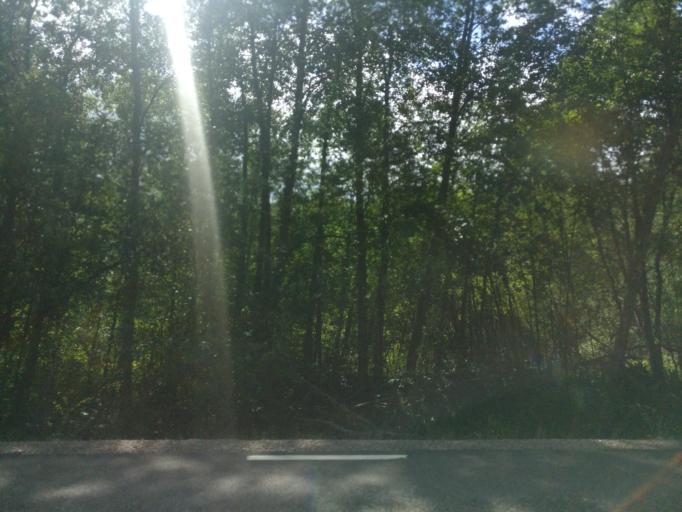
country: SE
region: Vaermland
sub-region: Hagfors Kommun
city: Ekshaerad
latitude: 60.3009
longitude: 13.3813
